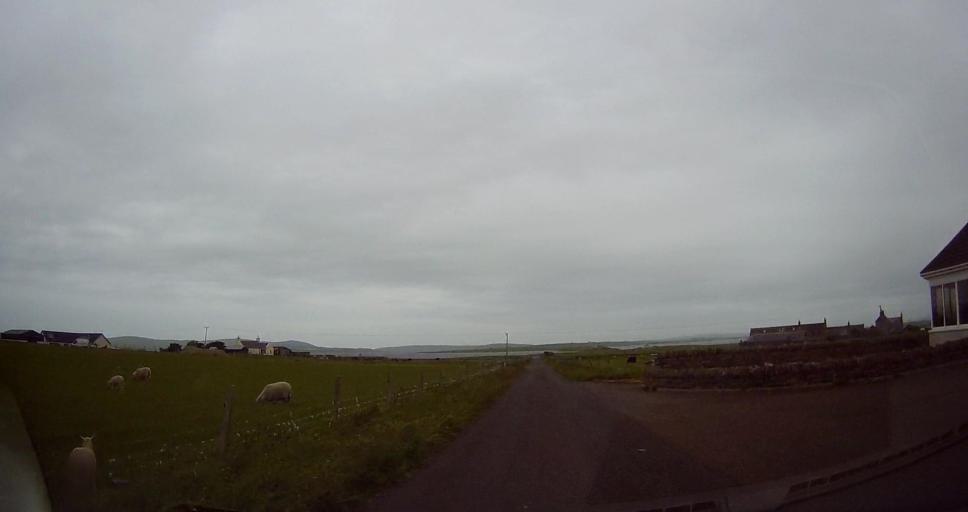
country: GB
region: Scotland
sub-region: Orkney Islands
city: Stromness
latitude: 58.9881
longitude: -3.1964
